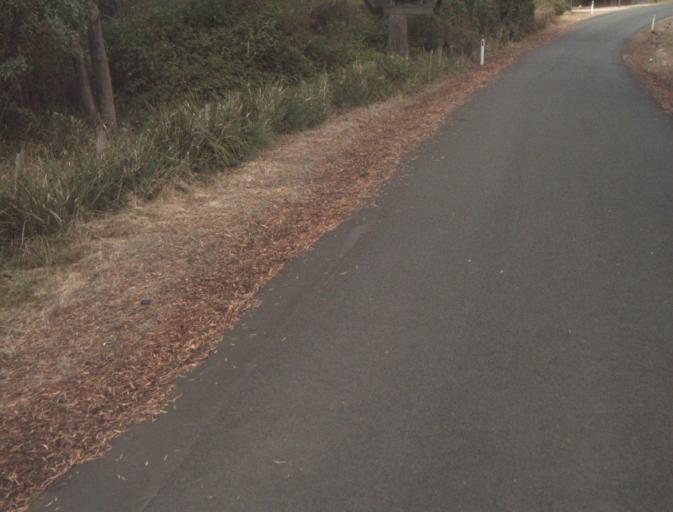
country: AU
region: Tasmania
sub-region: Launceston
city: Mayfield
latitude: -41.2821
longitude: 147.0411
